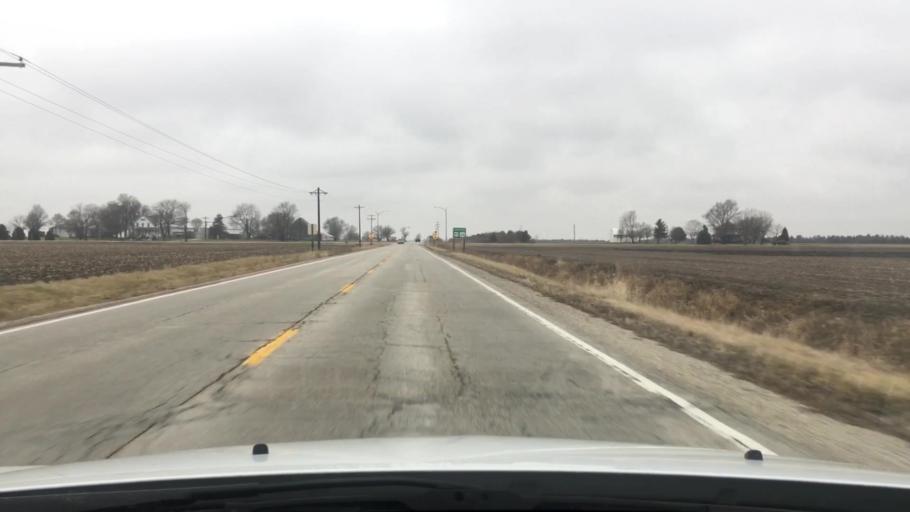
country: US
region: Illinois
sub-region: Iroquois County
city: Clifton
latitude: 40.8872
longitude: -87.8617
